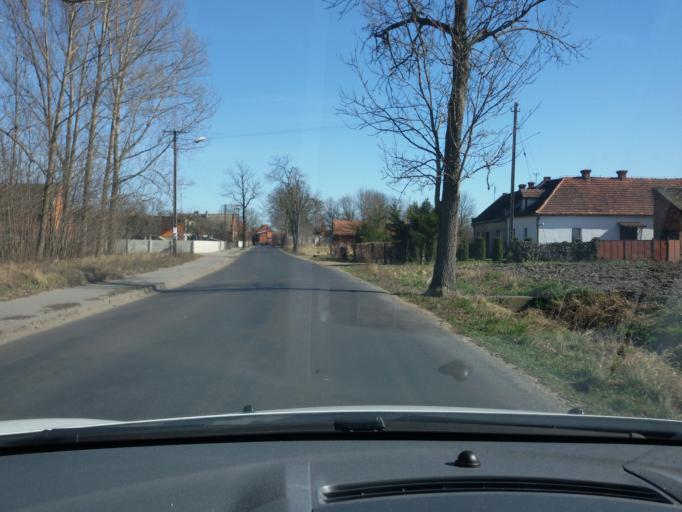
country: PL
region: Greater Poland Voivodeship
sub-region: Powiat gostynski
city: Poniec
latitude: 51.7512
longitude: 16.8490
